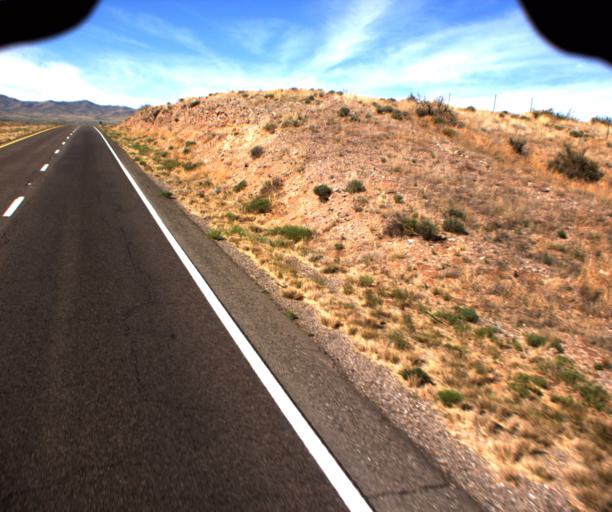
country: US
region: Arizona
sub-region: Cochise County
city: Willcox
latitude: 32.3700
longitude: -109.6758
